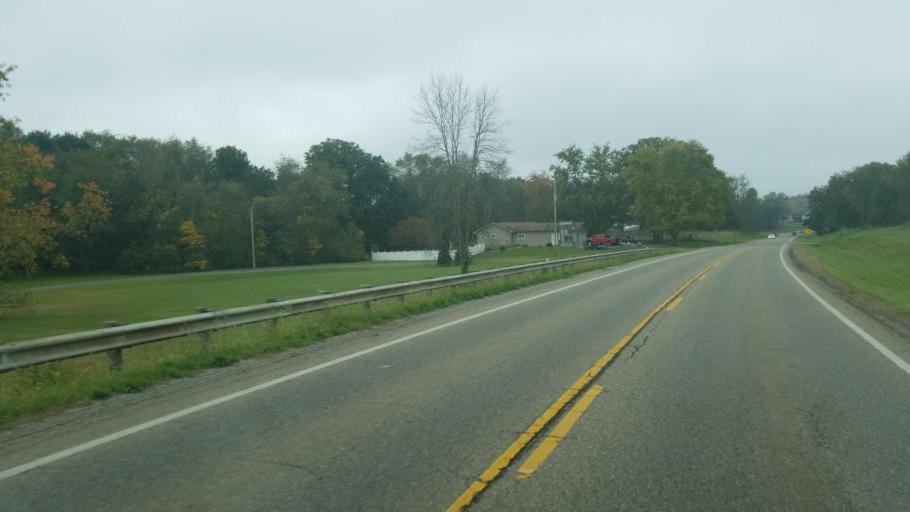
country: US
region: Ohio
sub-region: Carroll County
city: Lake Mohawk
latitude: 40.6470
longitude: -81.3076
